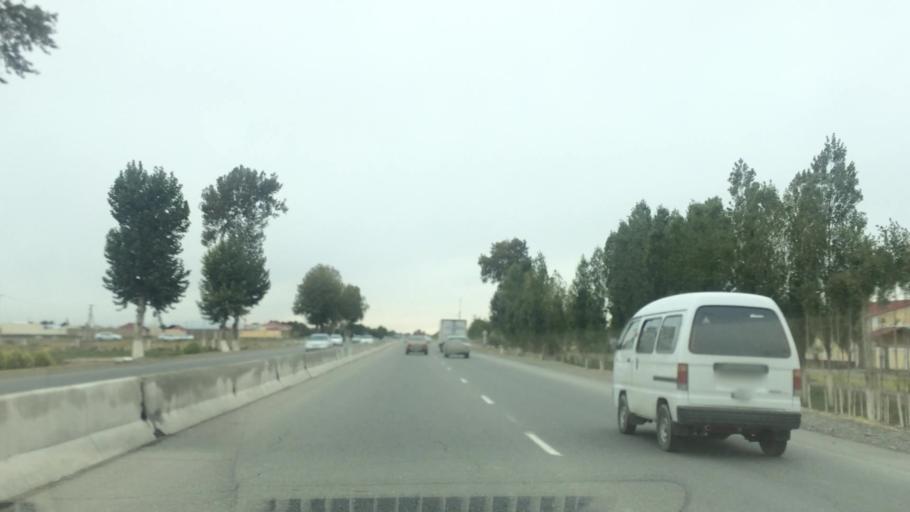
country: UZ
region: Samarqand
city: Jomboy
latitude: 39.7276
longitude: 67.1446
